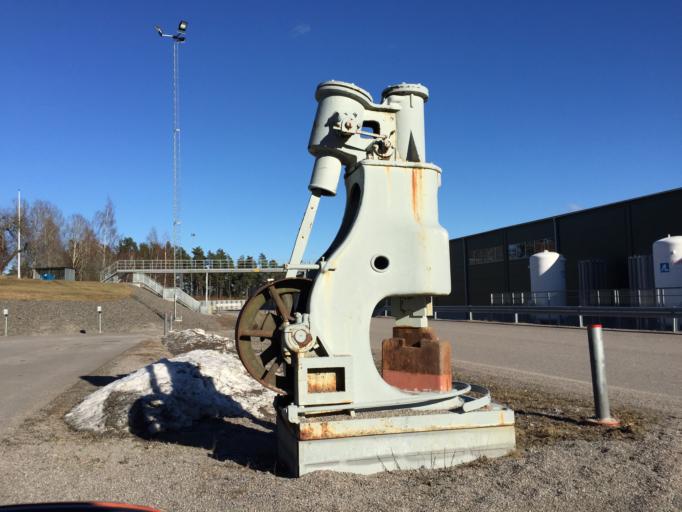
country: SE
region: Soedermanland
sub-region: Vingakers Kommun
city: Vingaker
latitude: 58.9168
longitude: 15.8707
